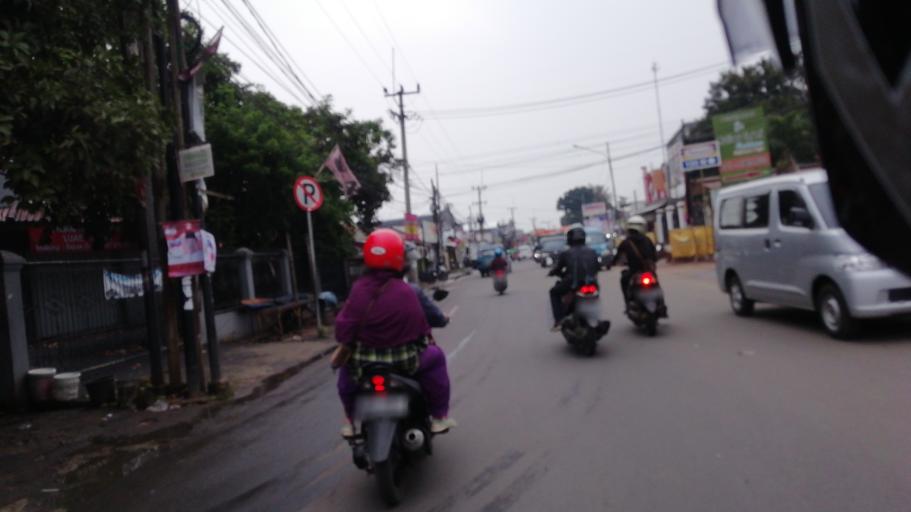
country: ID
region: West Java
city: Cibinong
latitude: -6.5135
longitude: 106.8073
